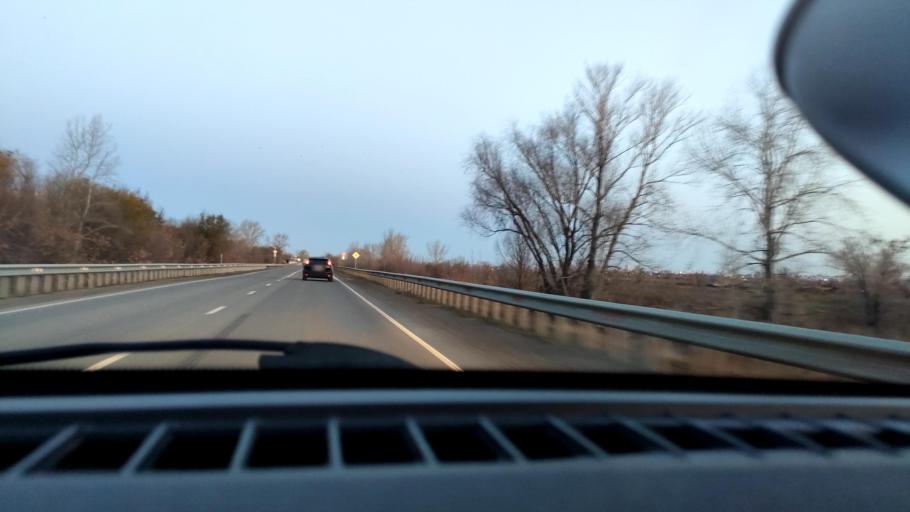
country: RU
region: Samara
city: Samara
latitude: 53.1109
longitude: 50.1302
